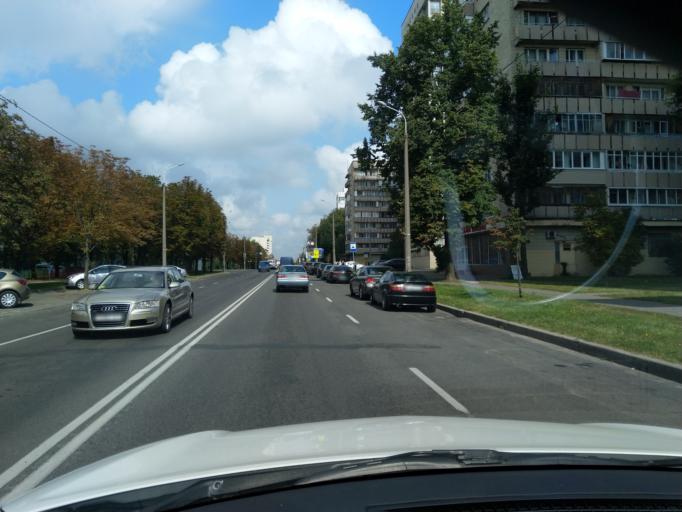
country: BY
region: Minsk
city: Minsk
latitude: 53.8973
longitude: 27.5876
